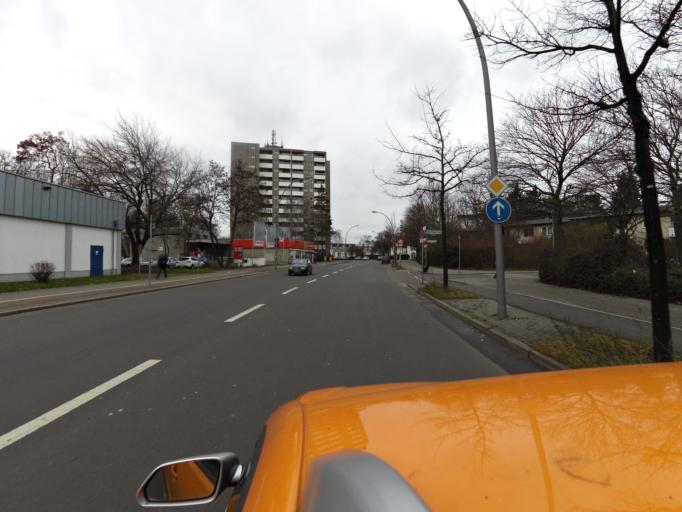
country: DE
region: Berlin
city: Britz
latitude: 52.4397
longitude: 13.4370
